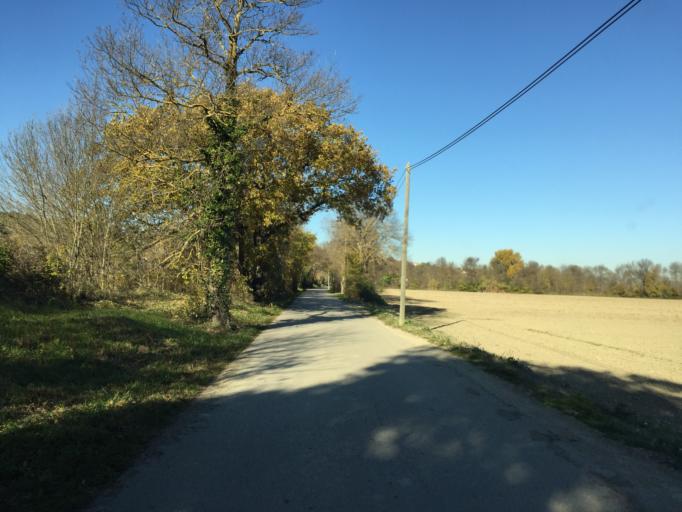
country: FR
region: Provence-Alpes-Cote d'Azur
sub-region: Departement du Vaucluse
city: Bedarrides
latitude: 44.0279
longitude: 4.9040
